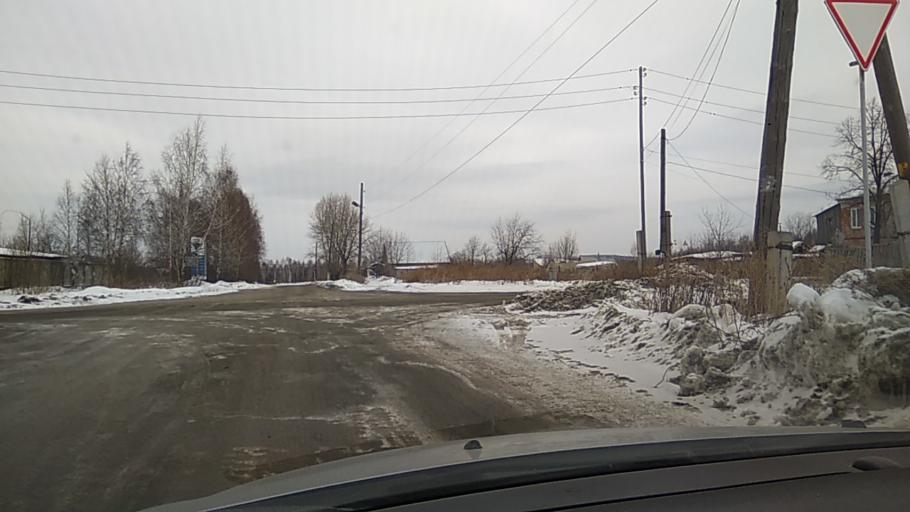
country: RU
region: Sverdlovsk
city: Revda
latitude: 56.8104
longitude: 59.9359
